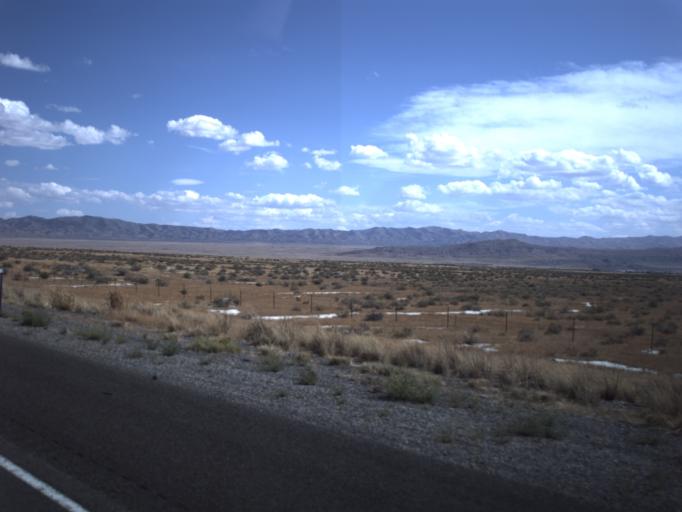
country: US
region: Utah
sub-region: Tooele County
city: Grantsville
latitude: 40.7252
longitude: -113.1408
